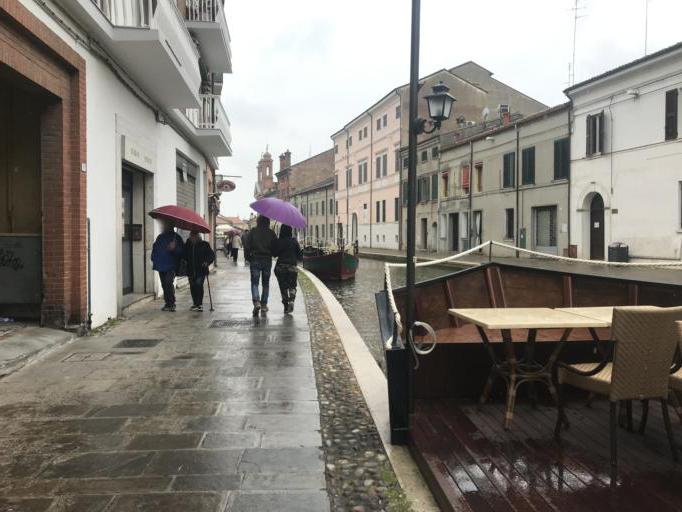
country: IT
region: Emilia-Romagna
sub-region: Provincia di Ferrara
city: Comacchio
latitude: 44.6944
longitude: 12.1826
